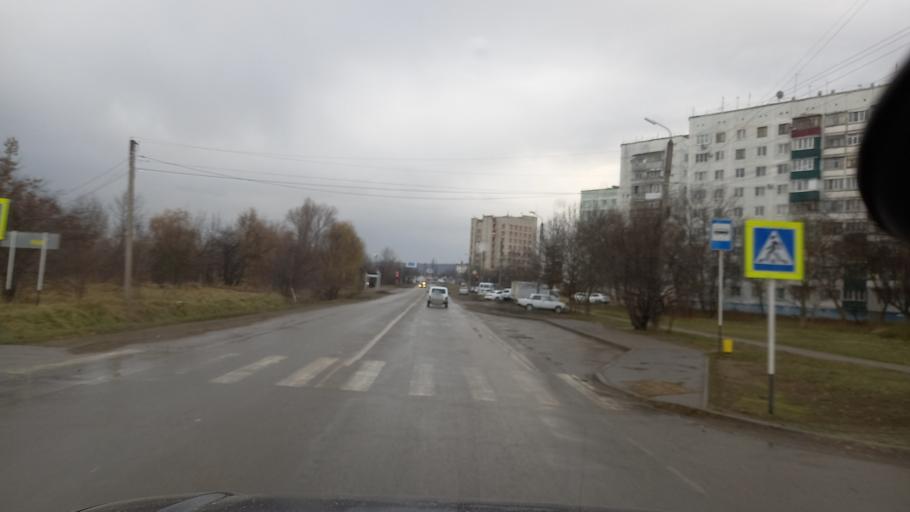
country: RU
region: Adygeya
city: Maykop
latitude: 44.5781
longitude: 40.1353
